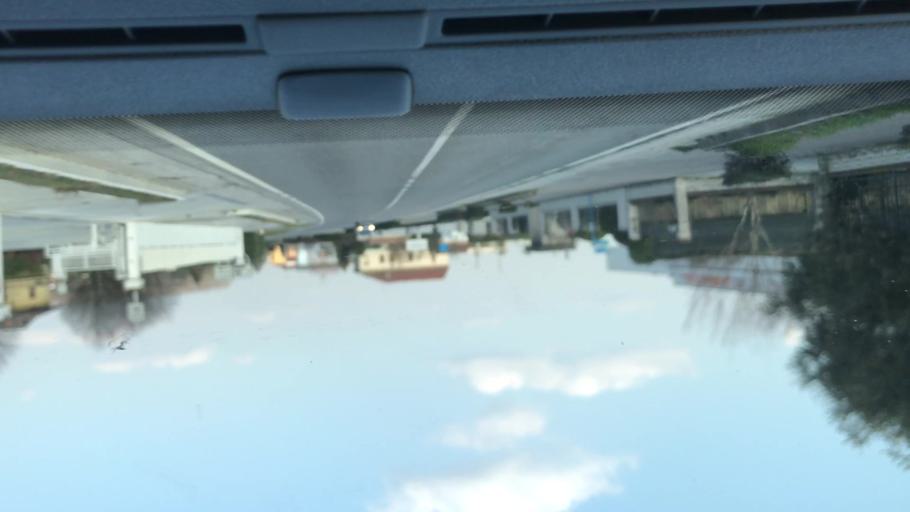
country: IT
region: Lombardy
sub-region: Provincia di Cremona
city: Vicomoscano
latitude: 44.9559
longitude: 10.4728
